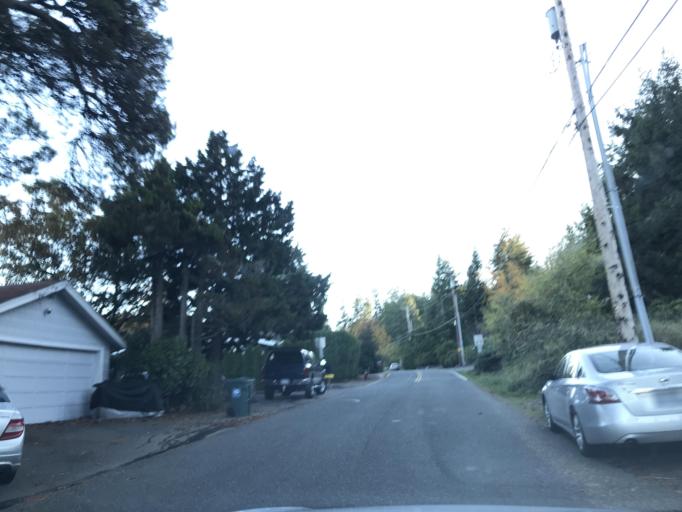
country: US
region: Washington
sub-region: Whatcom County
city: Geneva
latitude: 48.7537
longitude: -122.4123
